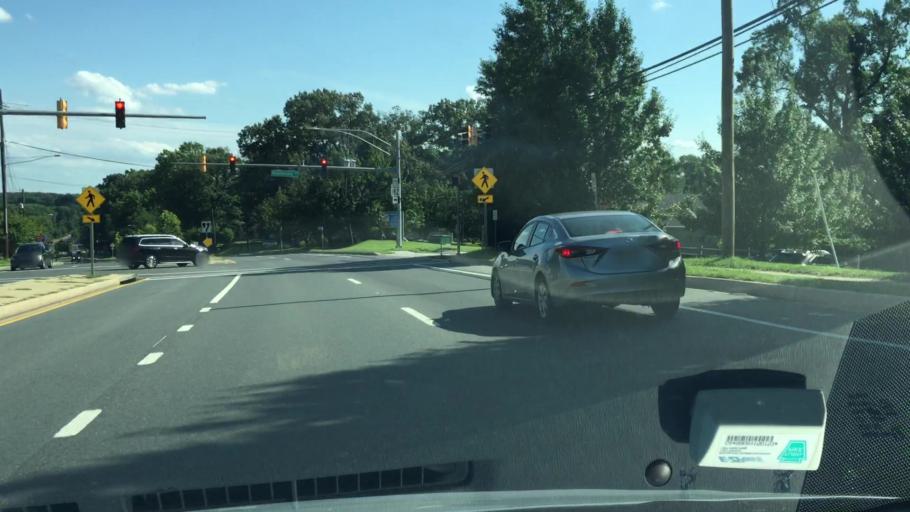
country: US
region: Maryland
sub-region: Montgomery County
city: Layhill
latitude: 39.0815
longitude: -77.0471
